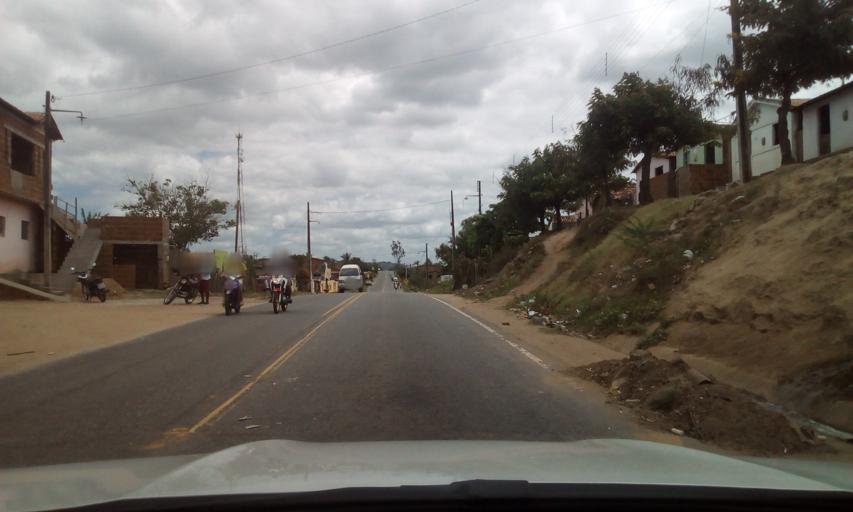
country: BR
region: Paraiba
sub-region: Serra Redonda
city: Alagoa Grande
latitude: -7.1848
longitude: -35.5888
